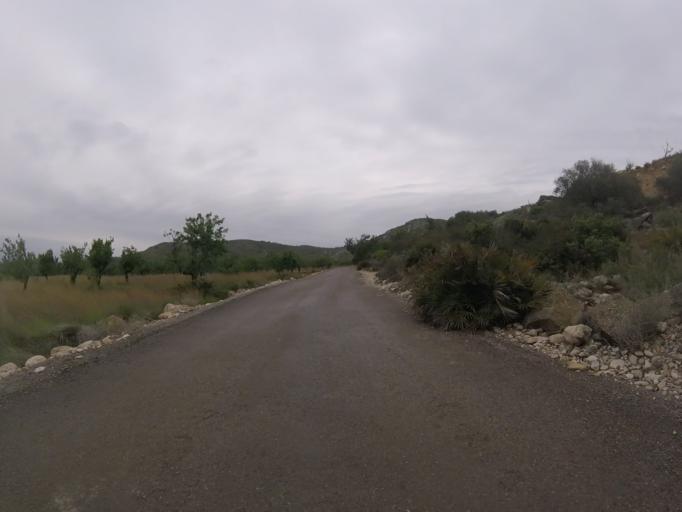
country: ES
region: Valencia
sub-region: Provincia de Castello
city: Alcala de Xivert
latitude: 40.2720
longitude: 0.2425
